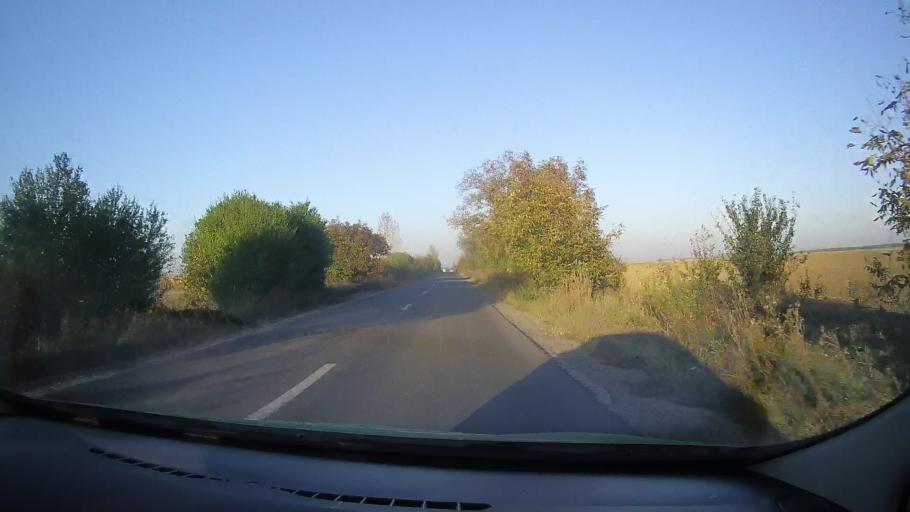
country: RO
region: Bihor
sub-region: Comuna Cetariu
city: Cetariu
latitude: 47.1853
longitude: 21.9858
